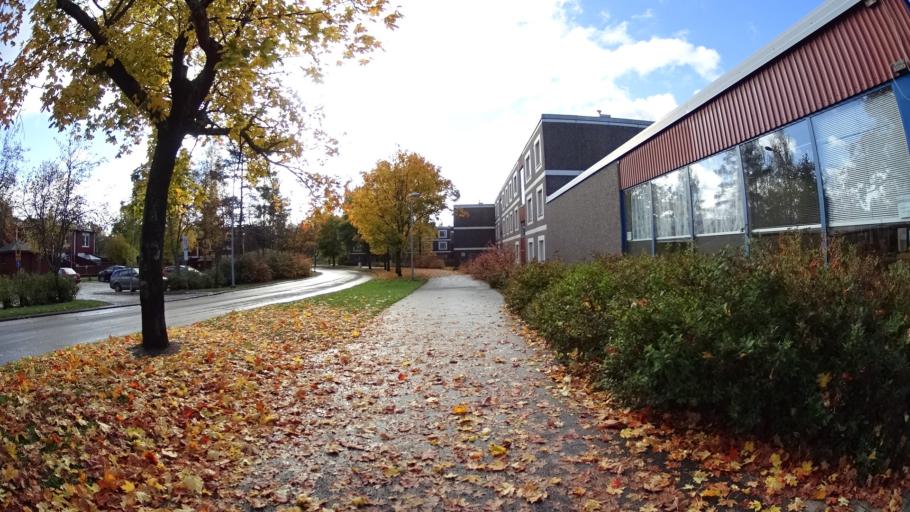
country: FI
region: Uusimaa
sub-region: Helsinki
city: Kilo
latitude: 60.2688
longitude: 24.8201
